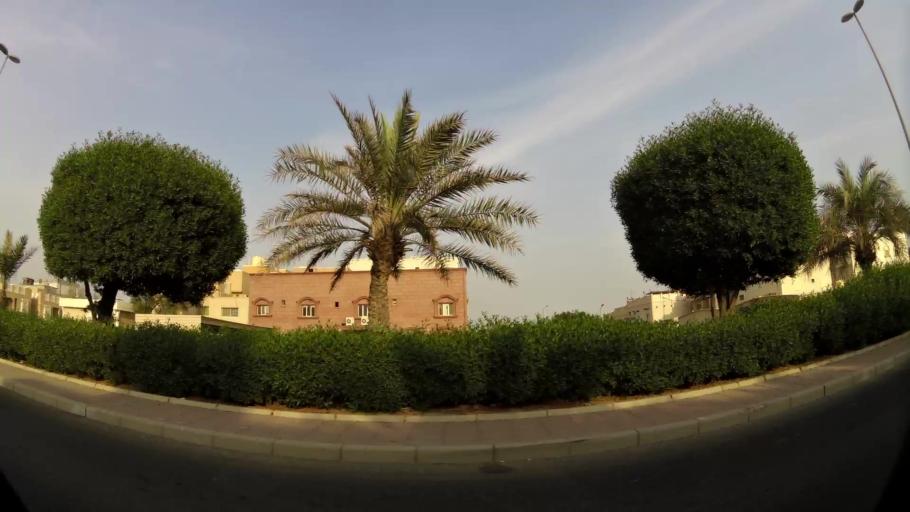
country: KW
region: Mubarak al Kabir
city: Mubarak al Kabir
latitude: 29.1917
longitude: 48.0700
